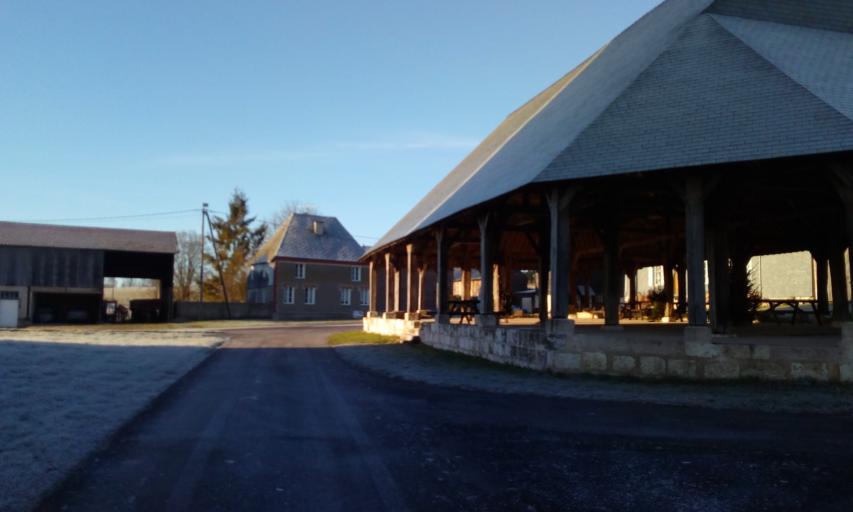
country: FR
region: Picardie
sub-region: Departement de l'Aisne
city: Rozoy-sur-Serre
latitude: 49.7245
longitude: 4.3082
